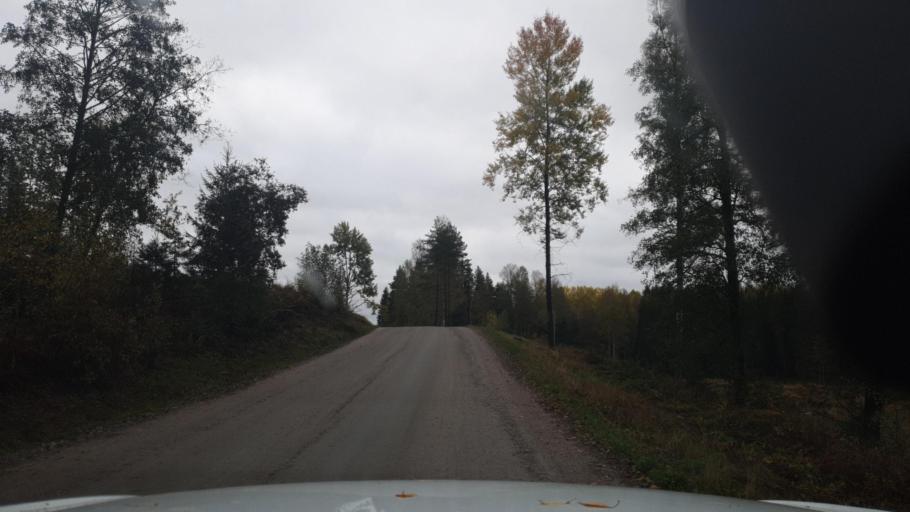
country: SE
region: Vaermland
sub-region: Karlstads Kommun
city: Edsvalla
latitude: 59.4938
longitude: 13.0297
